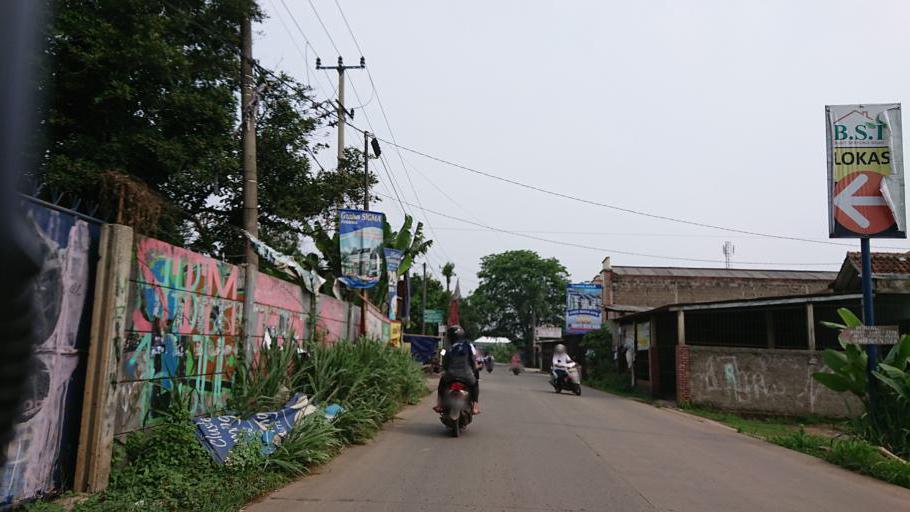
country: ID
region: West Java
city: Parung
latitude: -6.4074
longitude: 106.6945
